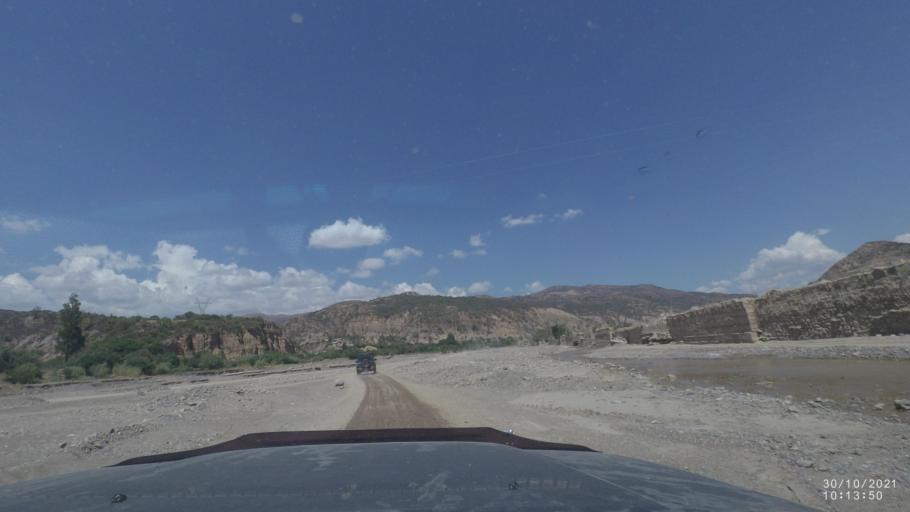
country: BO
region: Cochabamba
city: Sipe Sipe
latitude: -17.5716
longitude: -66.3581
